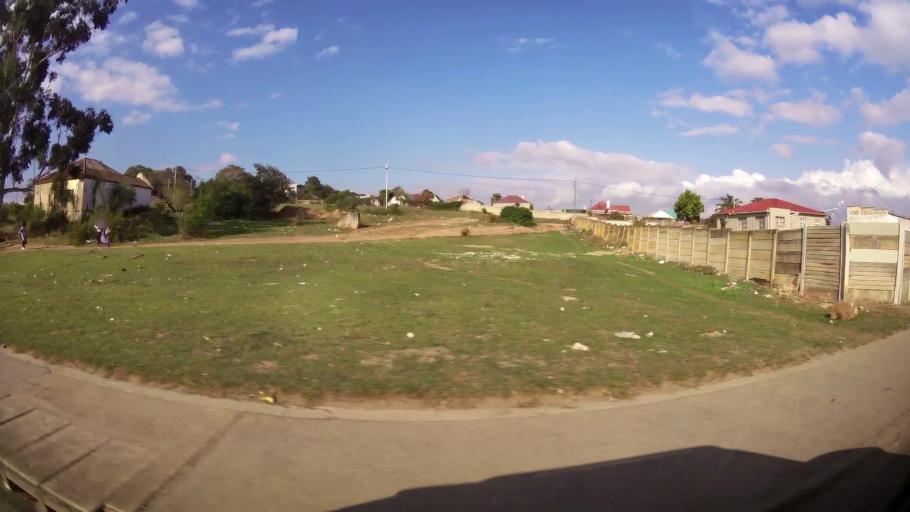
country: ZA
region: Eastern Cape
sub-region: Nelson Mandela Bay Metropolitan Municipality
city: Uitenhage
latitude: -33.7590
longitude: 25.3906
